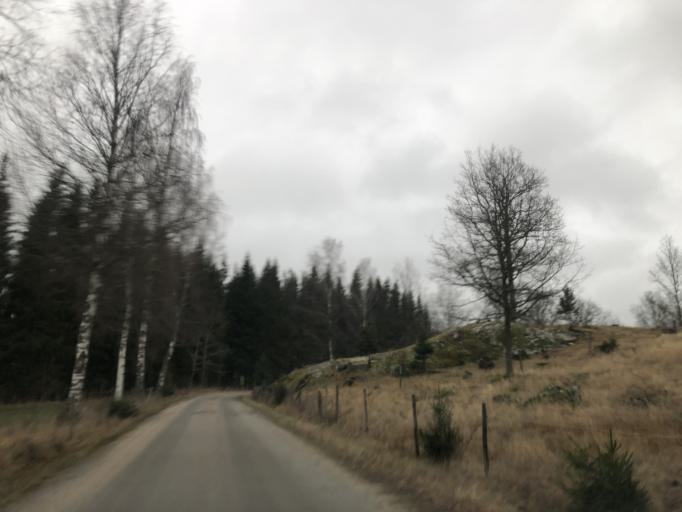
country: SE
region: Vaestra Goetaland
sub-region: Ulricehamns Kommun
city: Ulricehamn
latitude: 57.7965
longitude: 13.3857
